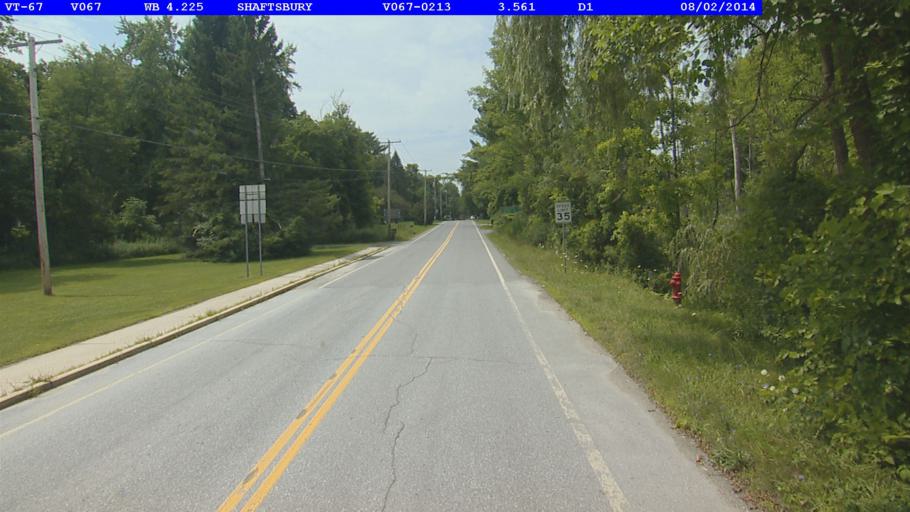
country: US
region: Vermont
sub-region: Bennington County
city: North Bennington
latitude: 42.9495
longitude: -73.2119
